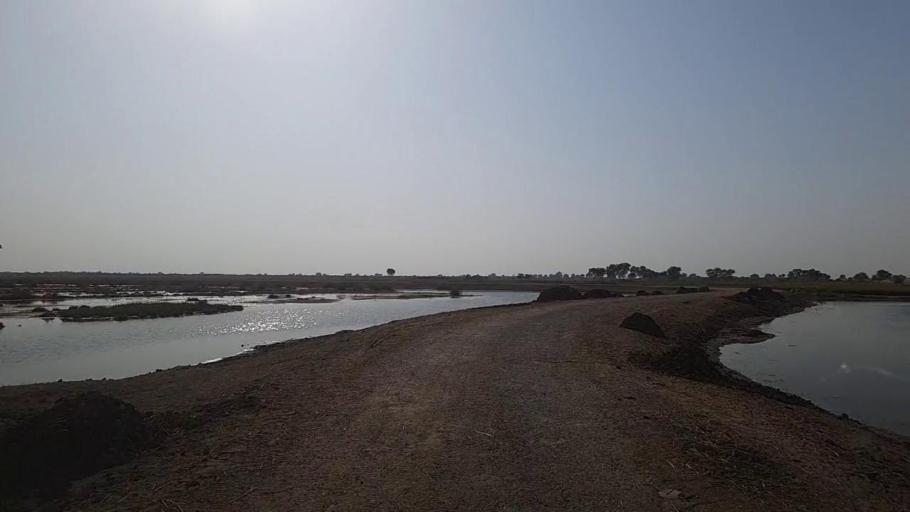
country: PK
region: Sindh
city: Kandhkot
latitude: 28.3672
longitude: 69.3310
